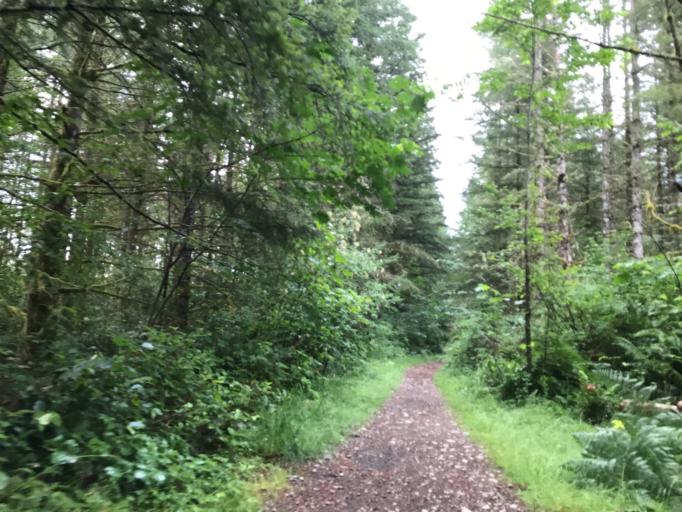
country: US
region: Washington
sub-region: King County
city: Ravensdale
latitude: 47.3472
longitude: -122.0084
